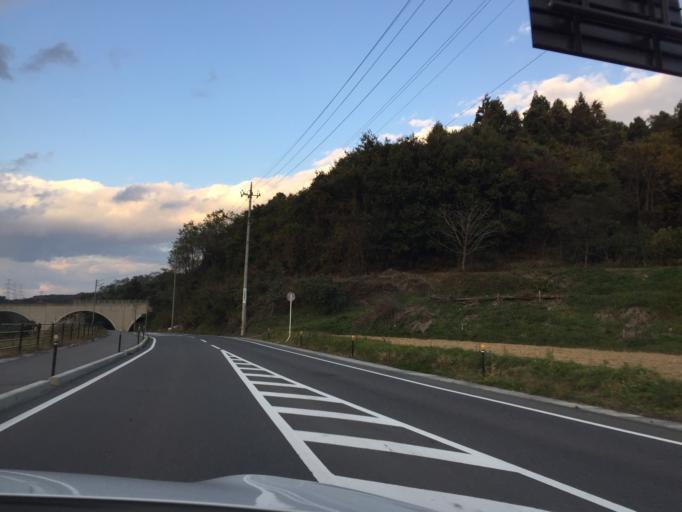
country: JP
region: Fukushima
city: Miharu
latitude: 37.4363
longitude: 140.4467
